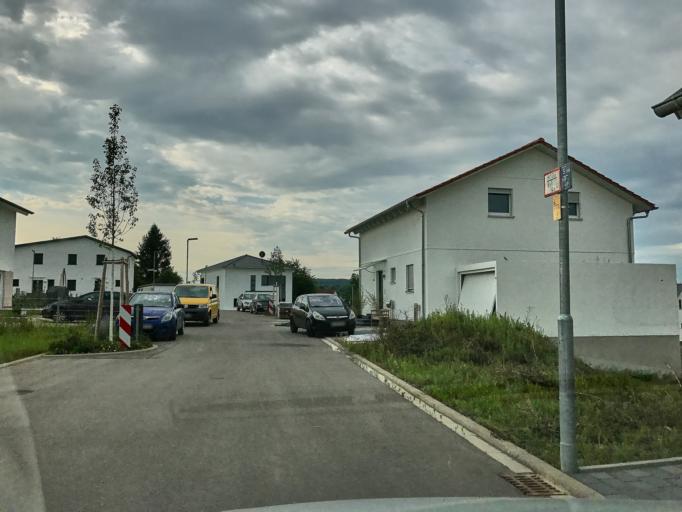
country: DE
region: Baden-Wuerttemberg
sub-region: Karlsruhe Region
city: Woessingen
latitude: 49.0172
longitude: 8.6018
